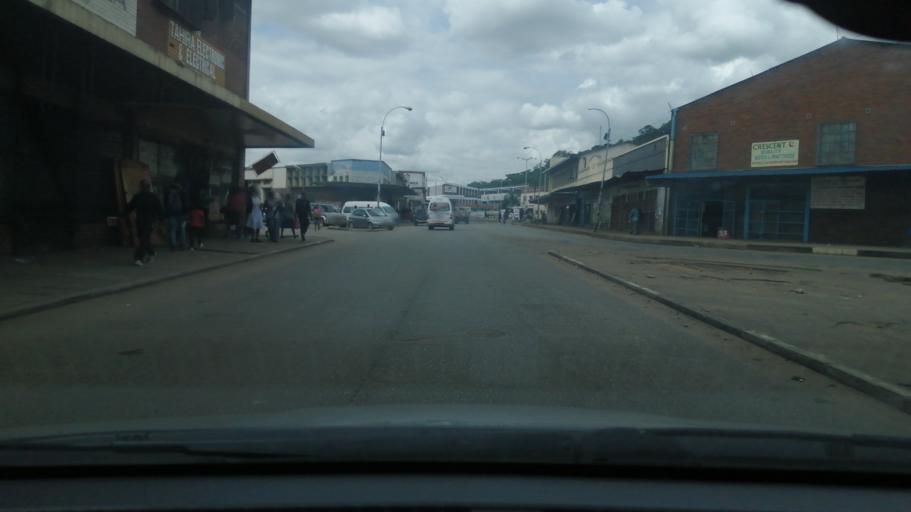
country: ZW
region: Harare
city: Harare
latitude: -17.8404
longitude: 31.0416
